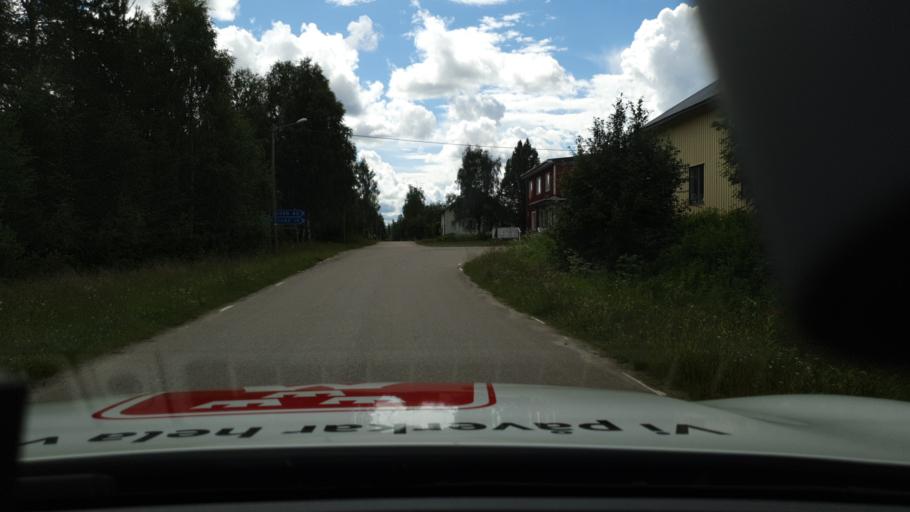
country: SE
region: Norrbotten
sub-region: Alvsbyns Kommun
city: AElvsbyn
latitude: 66.2780
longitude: 21.1228
